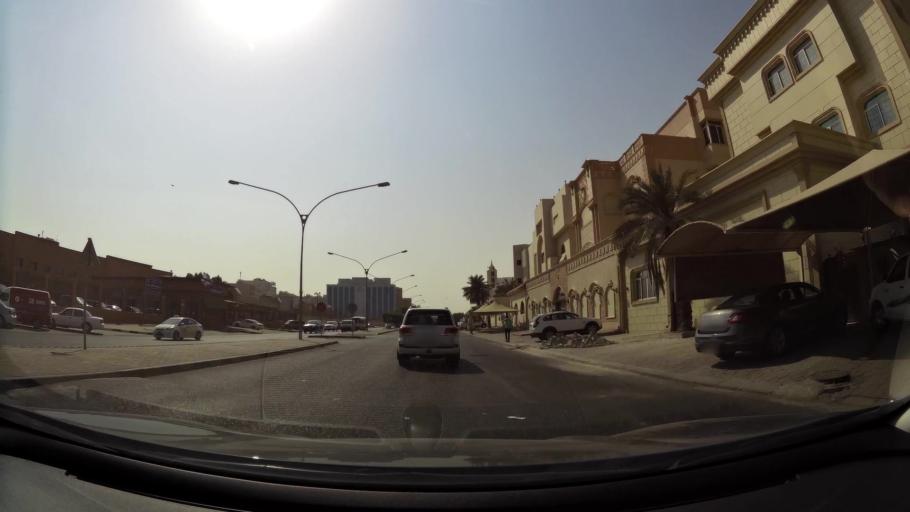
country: KW
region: Al Ahmadi
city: Al Fahahil
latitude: 29.0816
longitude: 48.1313
